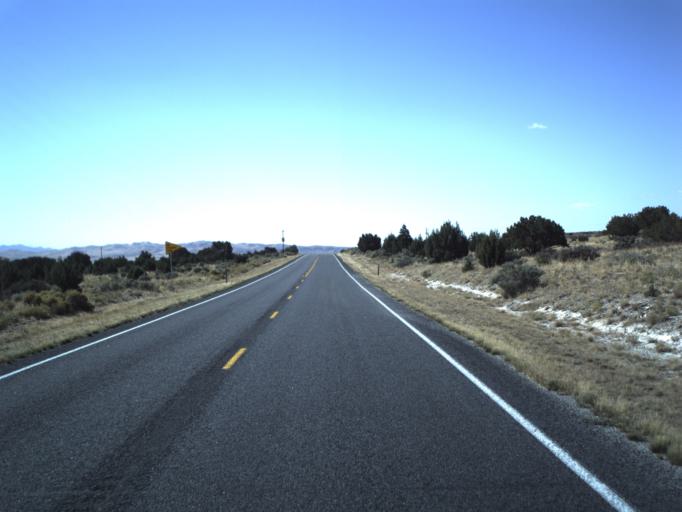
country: US
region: Utah
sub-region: Beaver County
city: Milford
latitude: 38.8393
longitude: -112.8461
